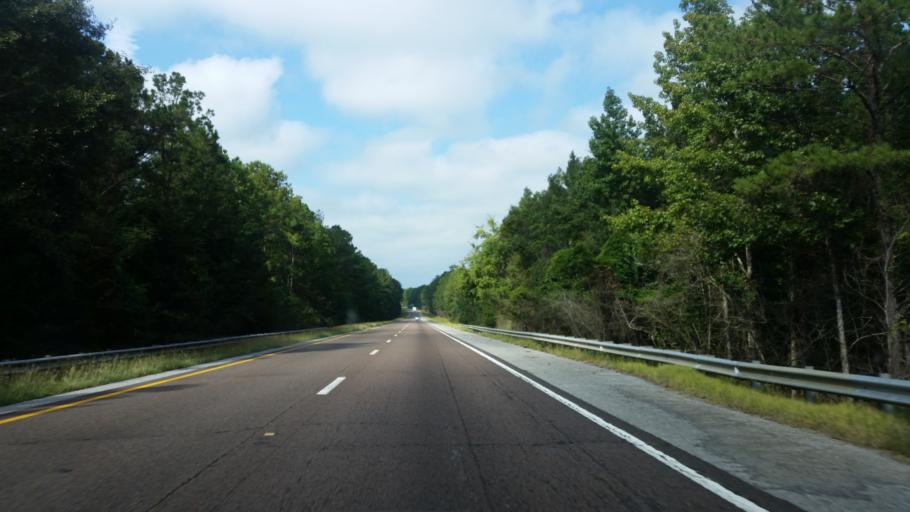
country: US
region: Alabama
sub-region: Baldwin County
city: Bay Minette
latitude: 30.9589
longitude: -87.7934
